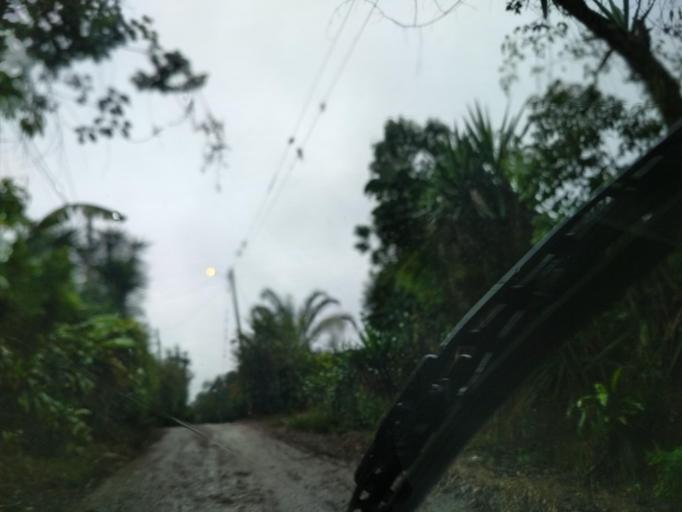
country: MX
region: Veracruz
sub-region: Amatlan de los Reyes
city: Centro de Readaptacion Social
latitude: 18.8279
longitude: -96.9354
